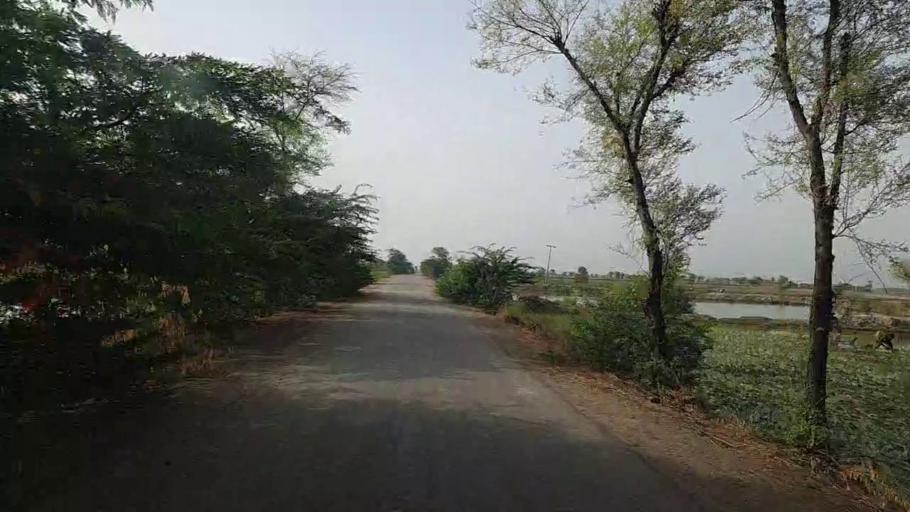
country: PK
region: Sindh
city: Khairpur Nathan Shah
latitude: 27.1076
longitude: 67.7923
